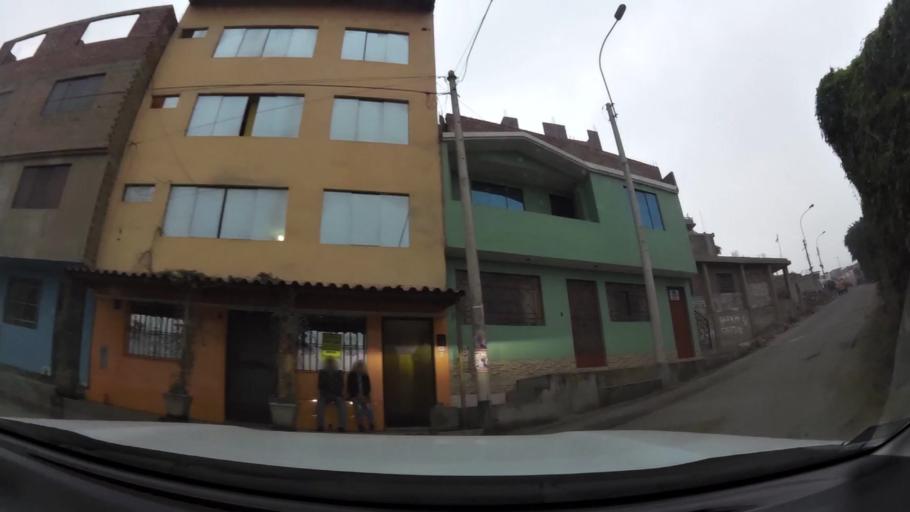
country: PE
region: Lima
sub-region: Lima
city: Surco
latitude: -12.1454
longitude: -76.9791
